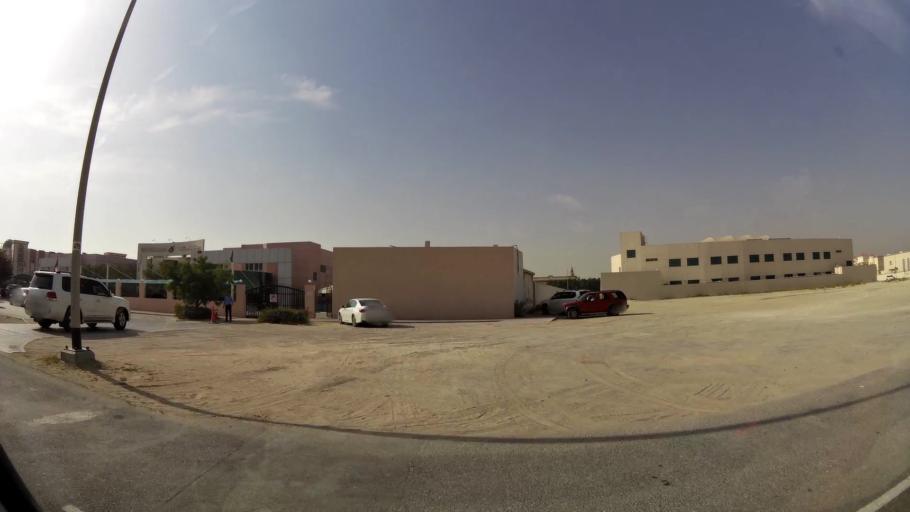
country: AE
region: Ash Shariqah
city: Sharjah
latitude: 25.2451
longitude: 55.4152
